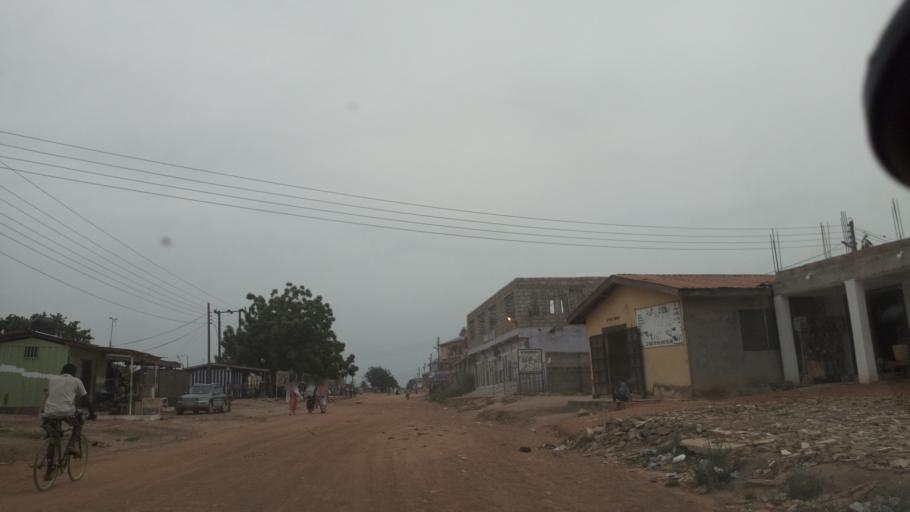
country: GH
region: Greater Accra
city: Medina Estates
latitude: 5.7079
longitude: -0.1315
